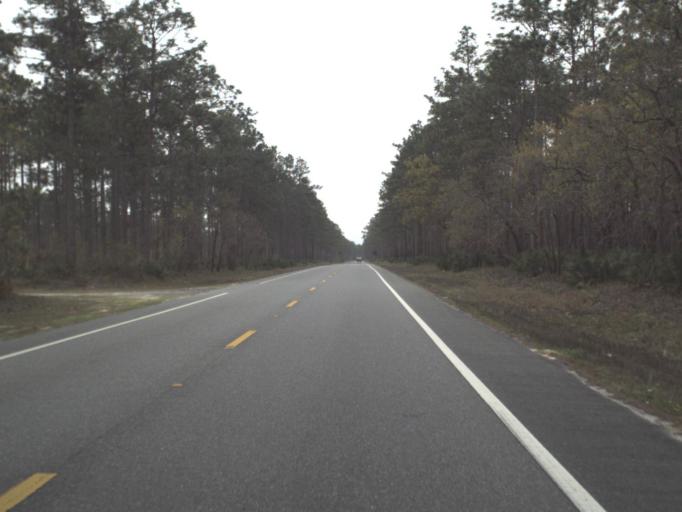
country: US
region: Florida
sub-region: Gulf County
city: Wewahitchka
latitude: 29.9881
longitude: -84.9763
